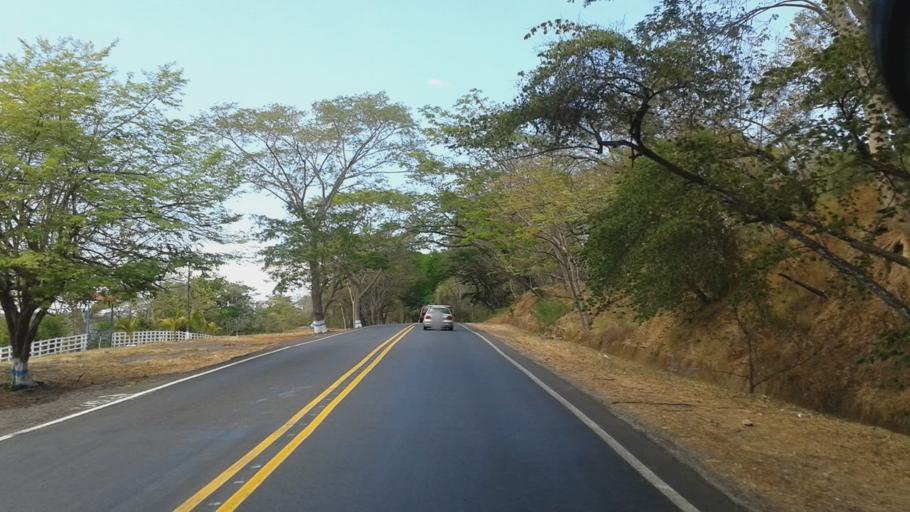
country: CR
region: Guanacaste
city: Juntas
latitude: 10.1419
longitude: -84.9080
